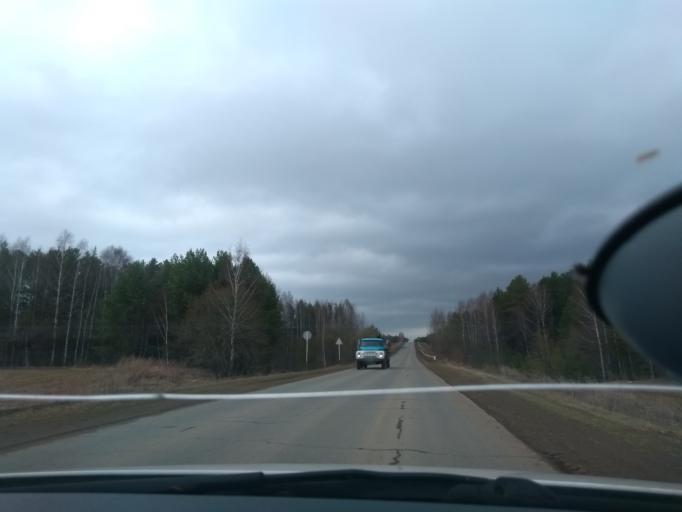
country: RU
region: Perm
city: Orda
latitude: 57.3436
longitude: 56.7874
